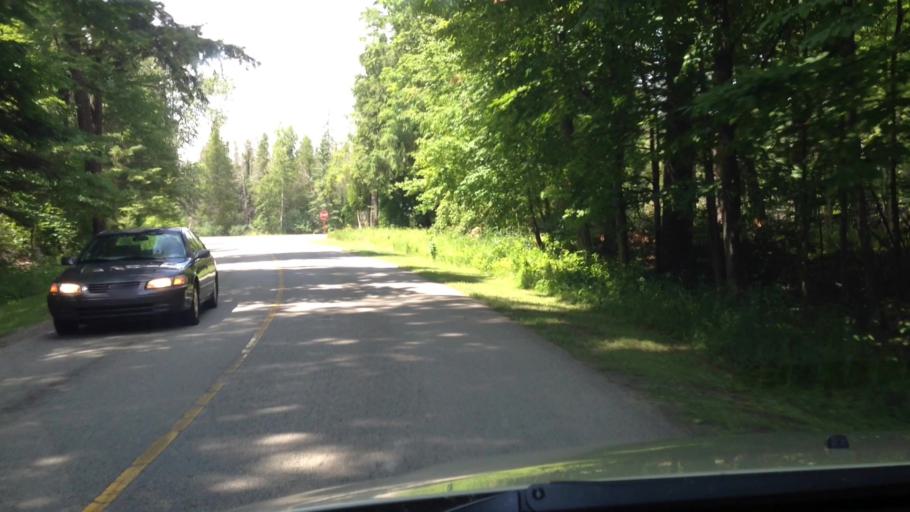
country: US
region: Michigan
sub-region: Menominee County
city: Menominee
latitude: 45.3950
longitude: -87.3661
